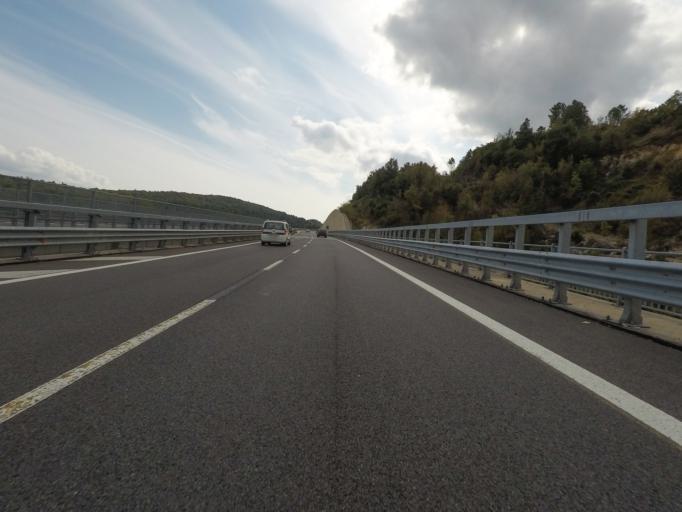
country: IT
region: Tuscany
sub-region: Provincia di Siena
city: Murlo
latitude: 43.1068
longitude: 11.2959
